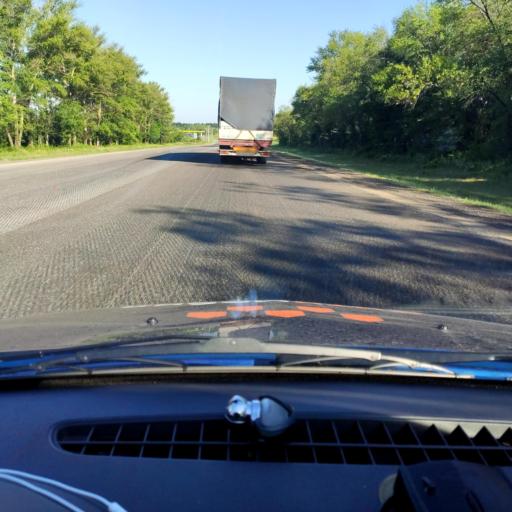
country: RU
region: Orjol
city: Zmiyevka
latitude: 52.7081
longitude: 36.3592
